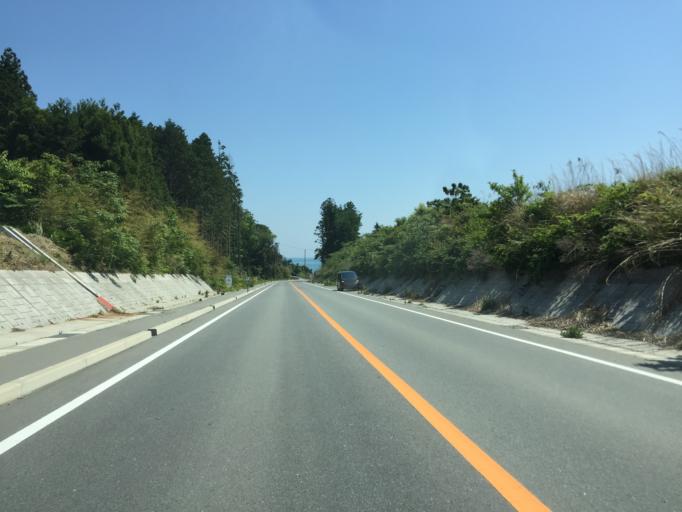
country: JP
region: Fukushima
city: Iwaki
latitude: 37.2194
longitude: 141.0074
